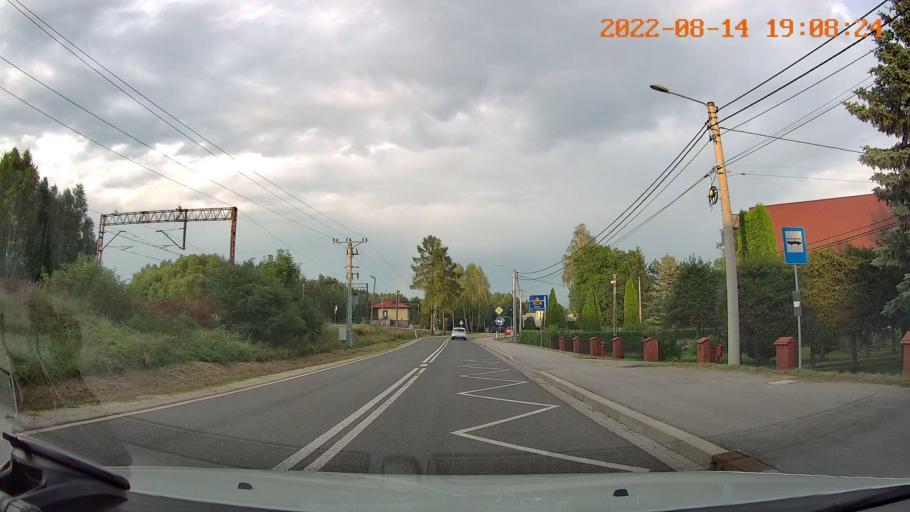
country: PL
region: Swietokrzyskie
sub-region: Powiat kielecki
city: Zagnansk
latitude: 50.9659
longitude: 20.7043
